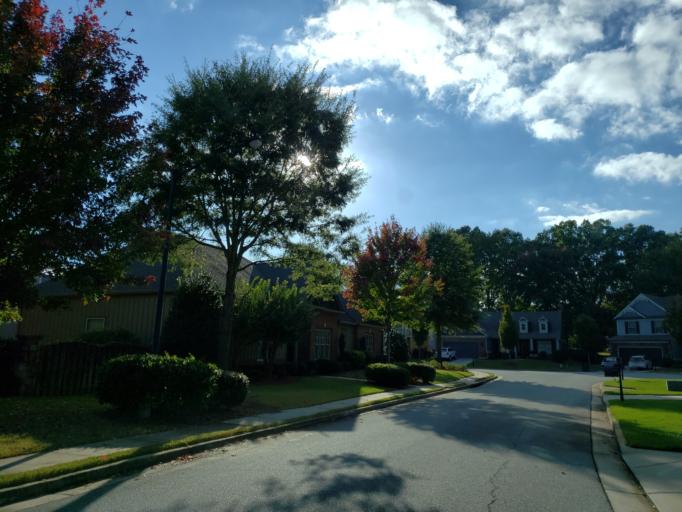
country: US
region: Georgia
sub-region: Cobb County
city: Marietta
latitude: 33.9905
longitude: -84.5049
